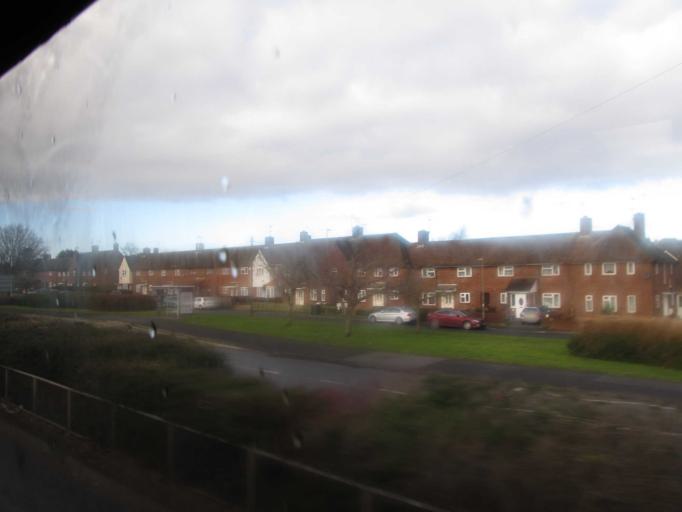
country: GB
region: England
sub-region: Hampshire
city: Basingstoke
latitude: 51.2540
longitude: -1.1058
